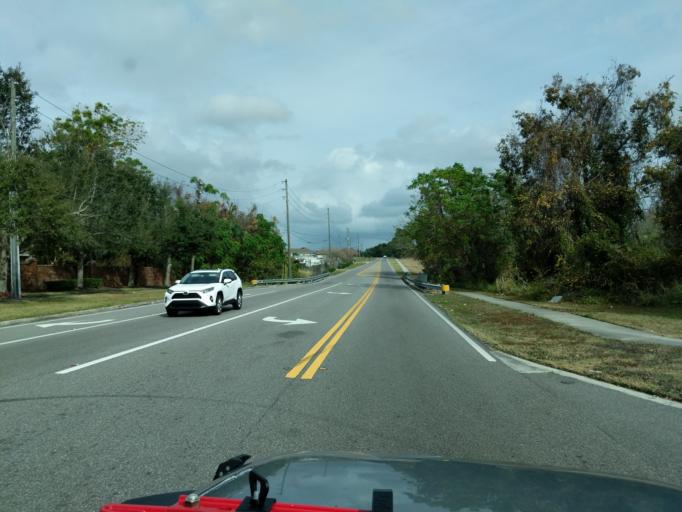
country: US
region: Florida
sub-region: Orange County
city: Paradise Heights
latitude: 28.6062
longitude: -81.5503
